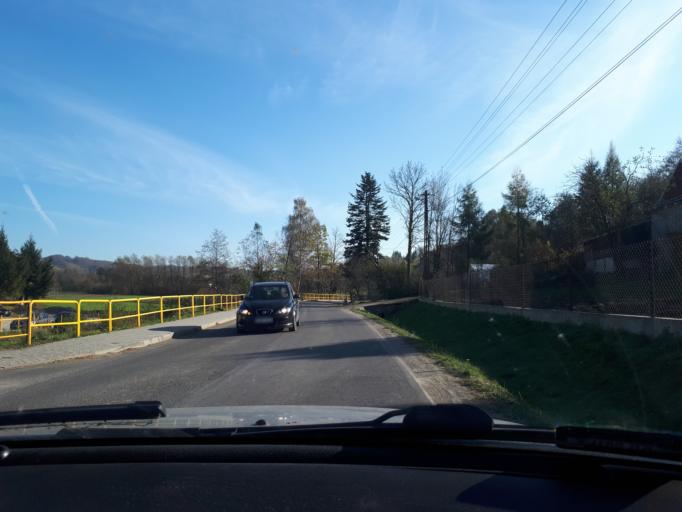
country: PL
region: Subcarpathian Voivodeship
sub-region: Powiat debicki
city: Debica
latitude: 49.9952
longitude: 21.4199
